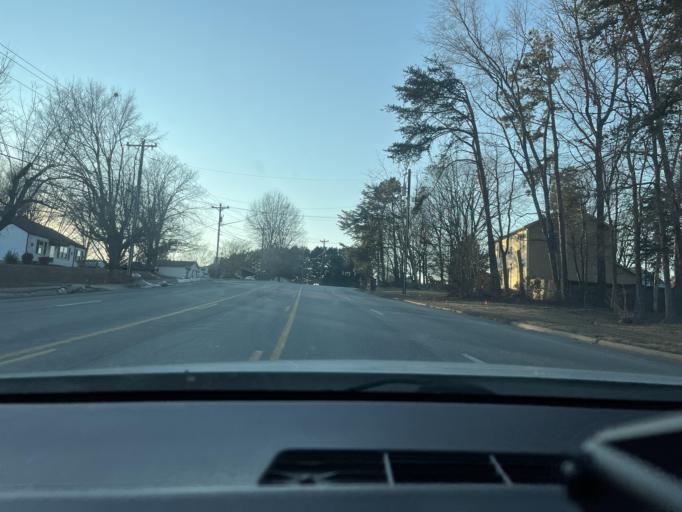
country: US
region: North Carolina
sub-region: Guilford County
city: Greensboro
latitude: 36.0175
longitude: -79.8161
